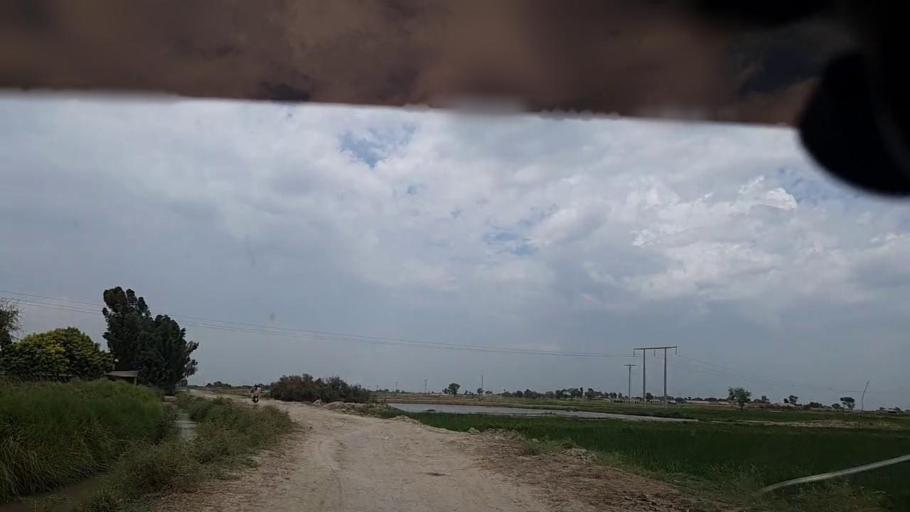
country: PK
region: Sindh
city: Ghauspur
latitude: 28.1105
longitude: 68.9861
